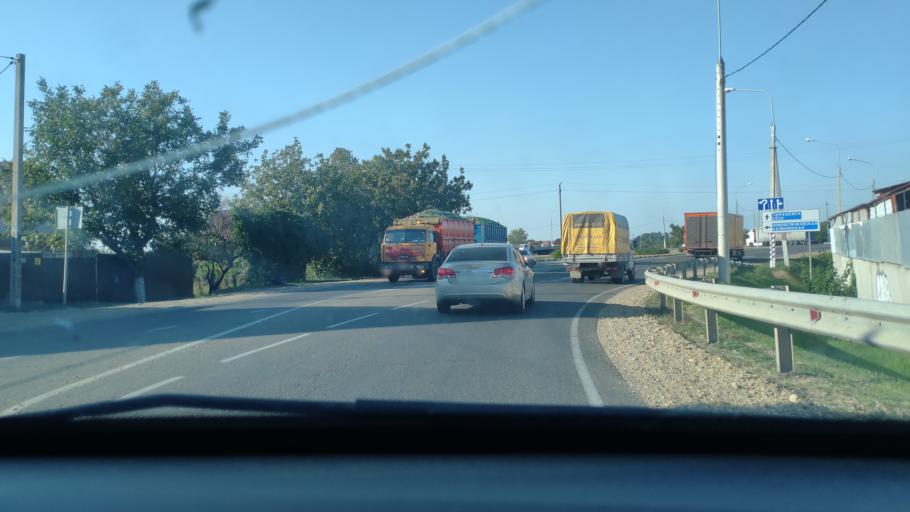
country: RU
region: Krasnodarskiy
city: Novotitarovskaya
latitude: 45.2506
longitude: 38.9947
